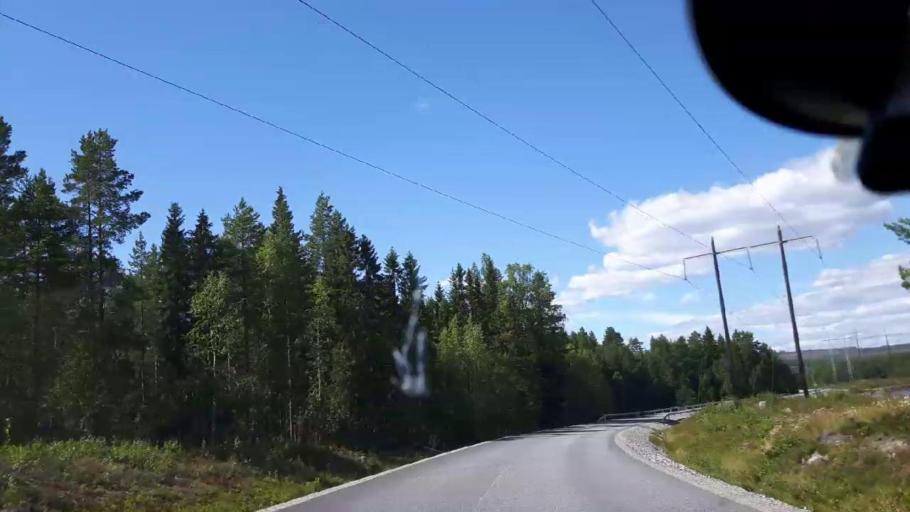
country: SE
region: Vaesternorrland
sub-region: Ange Kommun
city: Fransta
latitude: 62.6889
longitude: 16.3975
